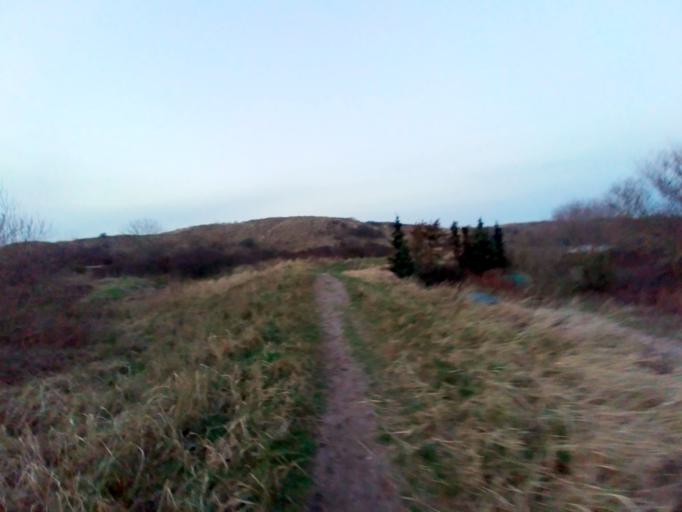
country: NL
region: North Holland
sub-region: Gemeente Bergen
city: Egmond aan Zee
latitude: 52.6225
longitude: 4.6442
